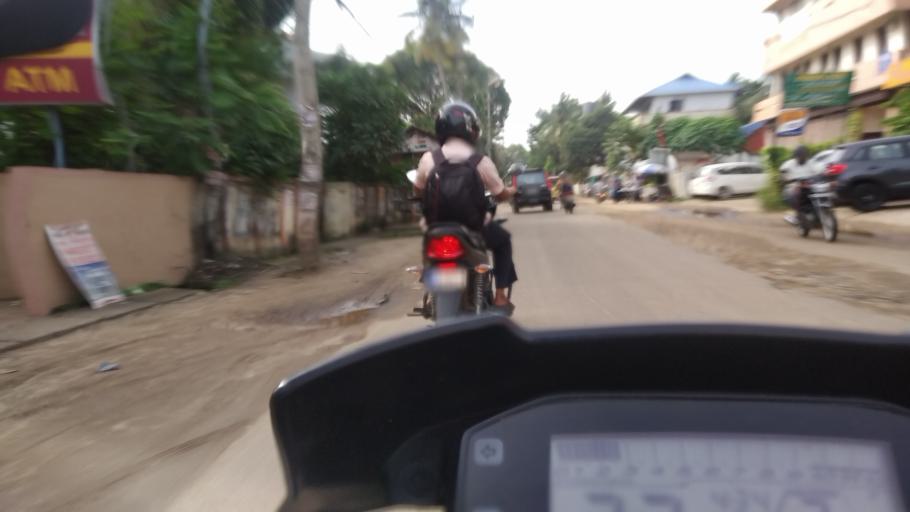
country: IN
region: Kerala
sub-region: Ernakulam
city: Cochin
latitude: 9.9805
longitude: 76.3135
